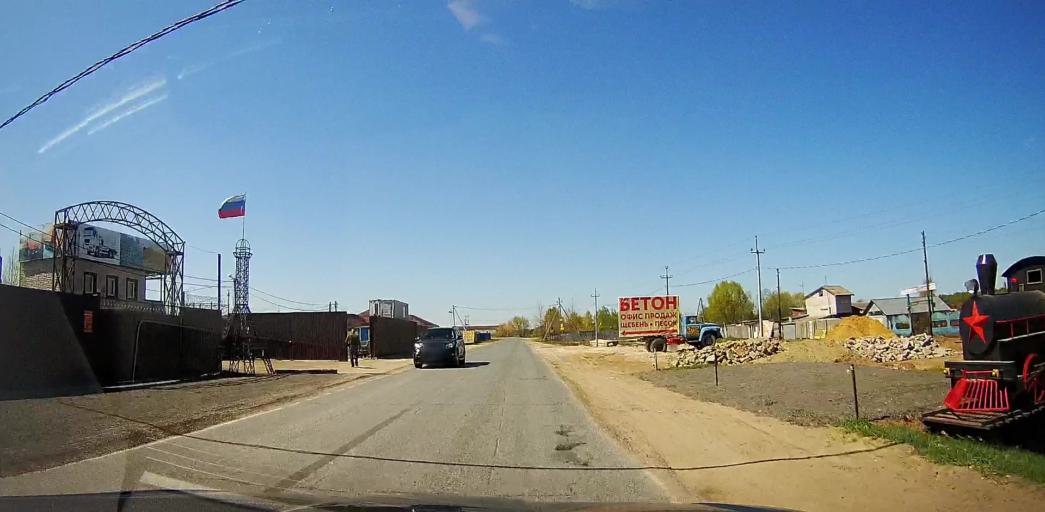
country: RU
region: Moskovskaya
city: Malyshevo
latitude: 55.4573
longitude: 38.3096
